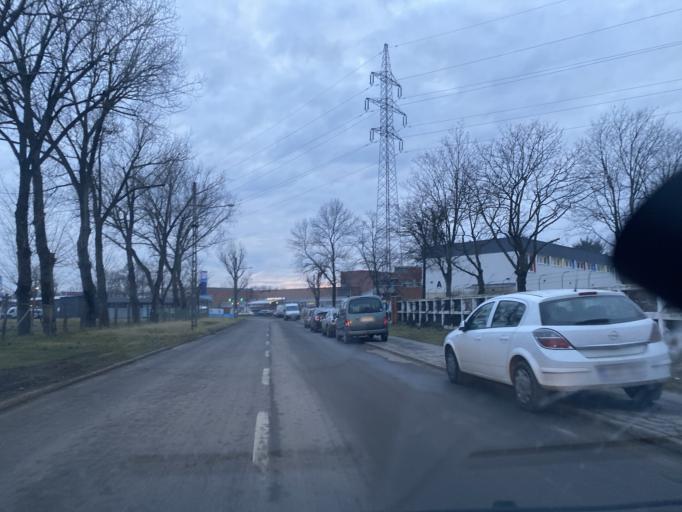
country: HU
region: Csongrad
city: Szeged
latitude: 46.2564
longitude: 20.1198
